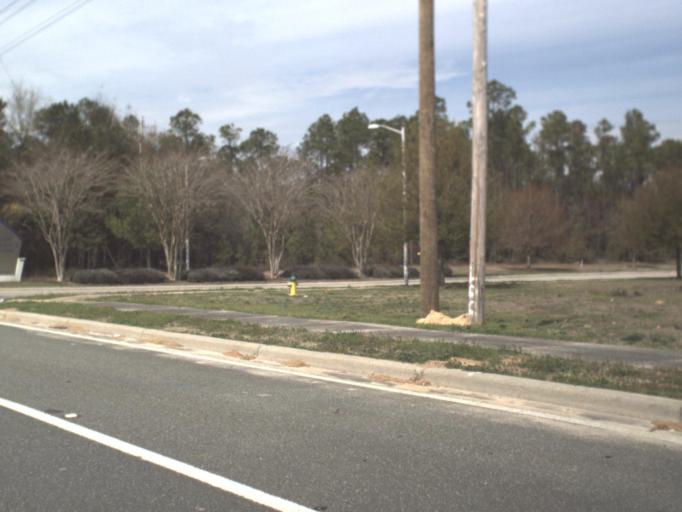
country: US
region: Florida
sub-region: Leon County
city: Tallahassee
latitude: 30.3980
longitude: -84.3303
